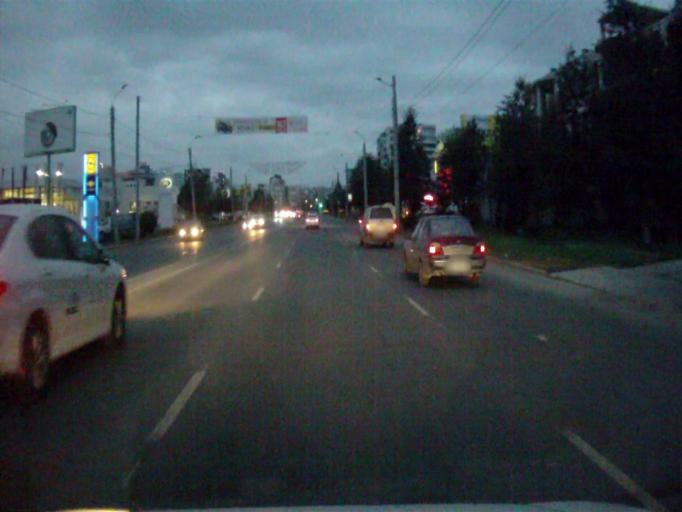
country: RU
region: Chelyabinsk
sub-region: Gorod Chelyabinsk
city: Chelyabinsk
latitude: 55.1719
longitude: 61.3009
